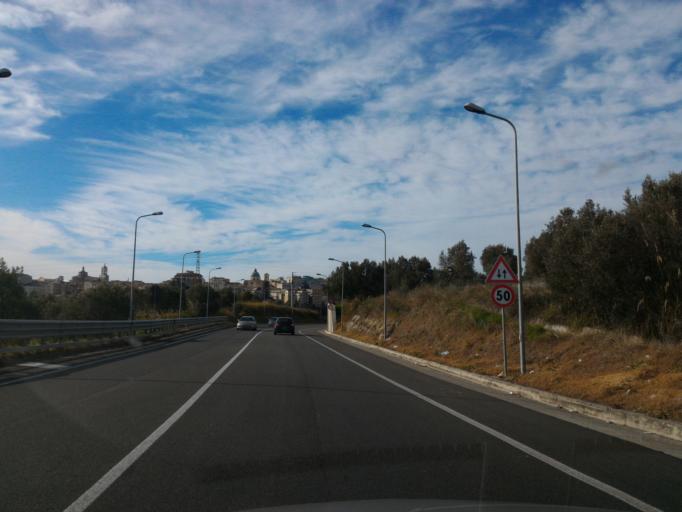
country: IT
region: Calabria
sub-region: Provincia di Catanzaro
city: Siano
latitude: 38.9116
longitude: 16.5999
